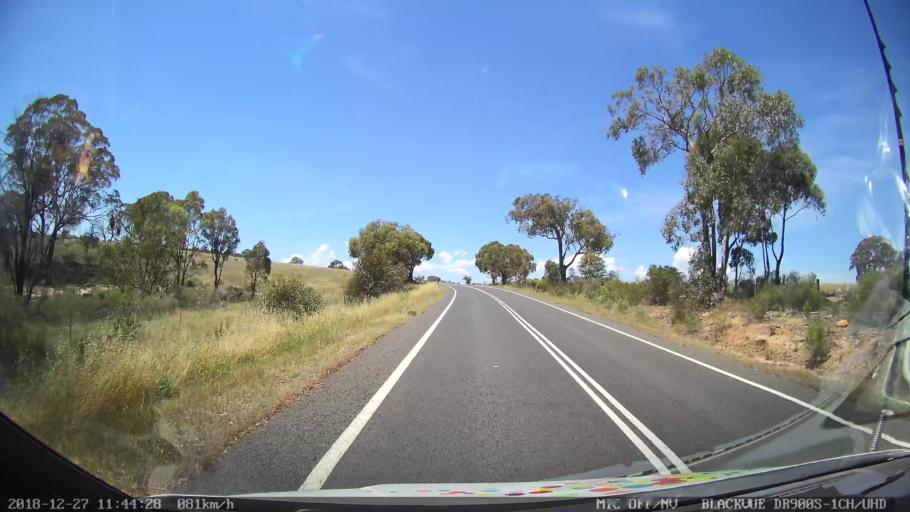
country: AU
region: New South Wales
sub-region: Bathurst Regional
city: Perthville
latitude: -33.5723
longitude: 149.4752
